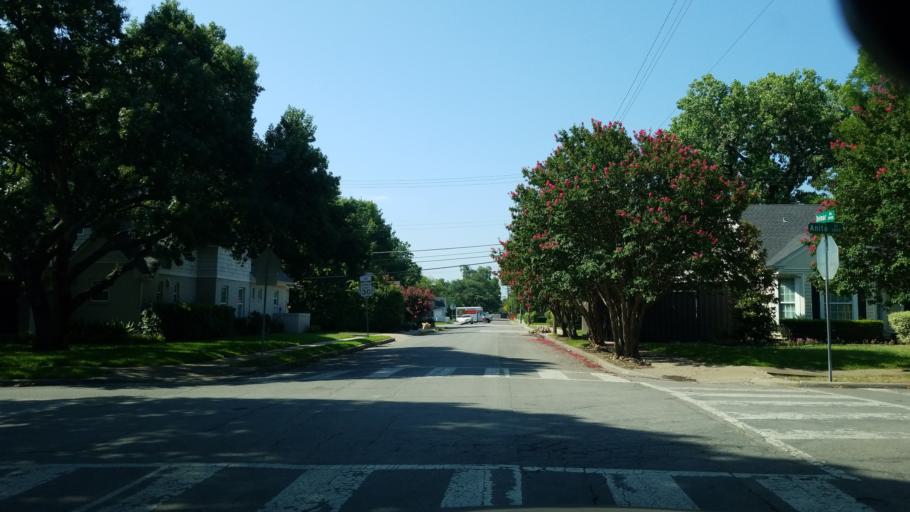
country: US
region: Texas
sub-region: Dallas County
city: Highland Park
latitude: 32.8348
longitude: -96.7657
